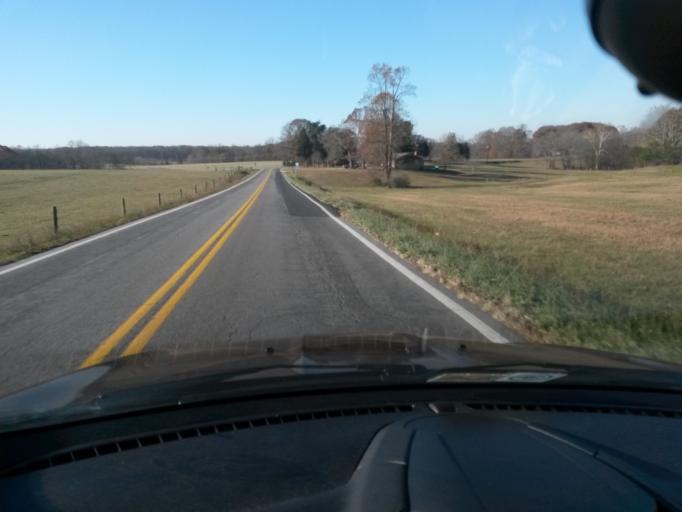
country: US
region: Virginia
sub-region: Charlotte County
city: Charlotte Court House
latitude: 37.1823
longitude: -78.6972
